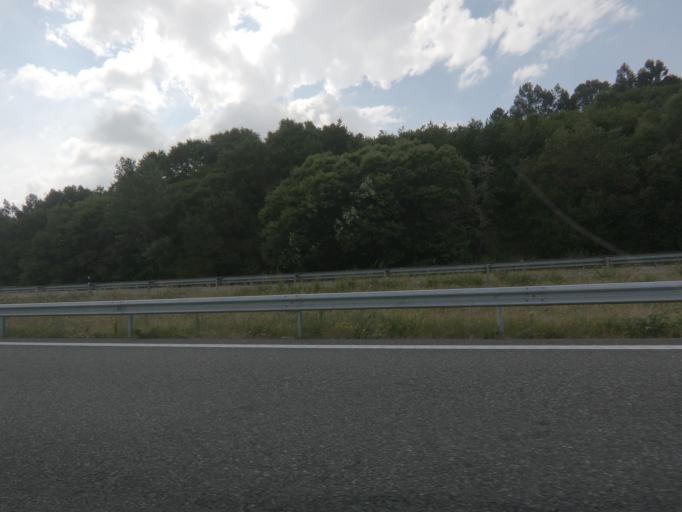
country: ES
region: Galicia
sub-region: Provincia de Ourense
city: Melon
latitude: 42.2347
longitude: -8.2308
